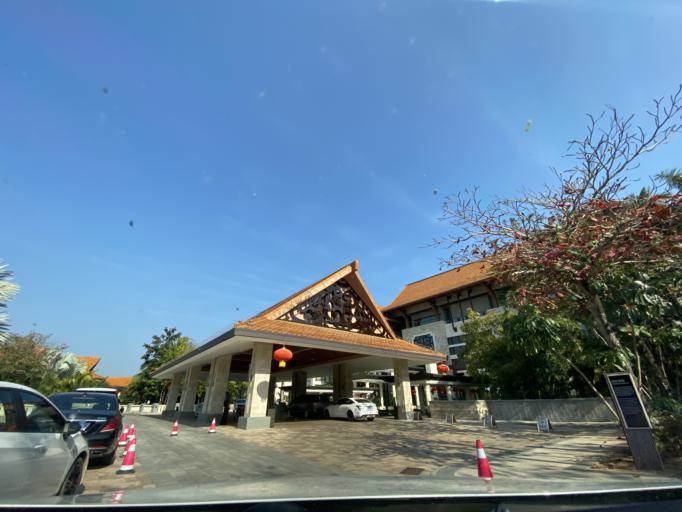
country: CN
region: Hainan
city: Haitangwan
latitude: 18.4023
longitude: 109.7800
